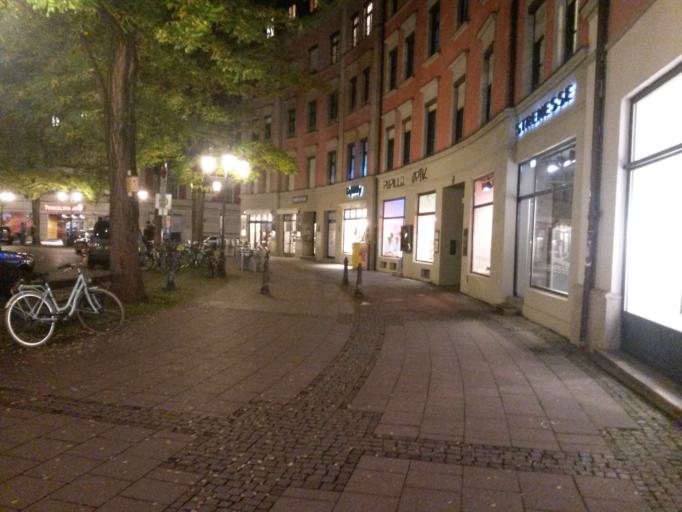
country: DE
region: Bavaria
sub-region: Upper Bavaria
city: Munich
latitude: 48.1317
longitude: 11.5761
